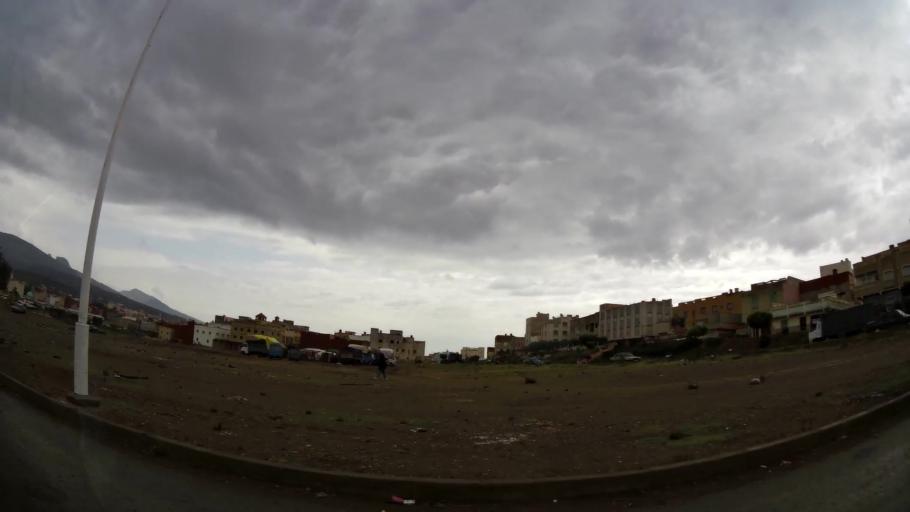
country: MA
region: Oriental
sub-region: Nador
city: Nador
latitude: 35.1484
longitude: -3.0046
